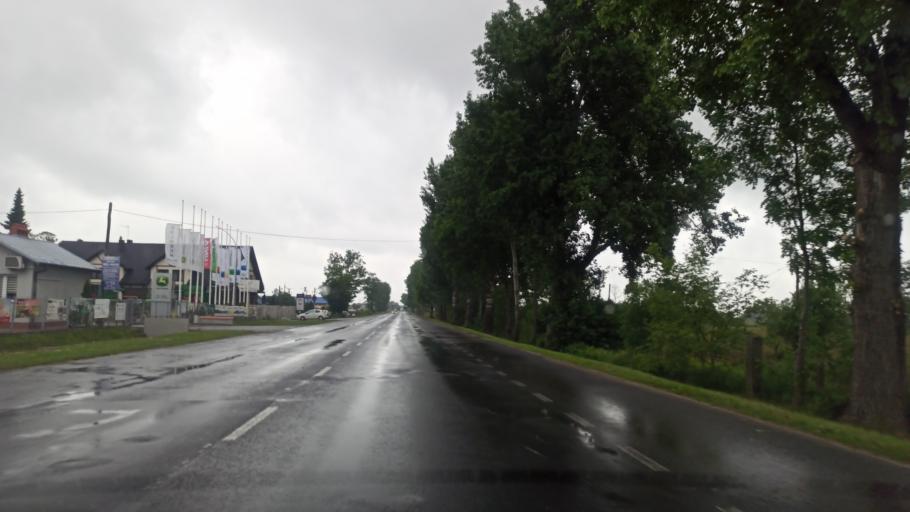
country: PL
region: Subcarpathian Voivodeship
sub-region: Powiat jaroslawski
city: Radymno
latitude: 49.9561
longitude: 22.8112
